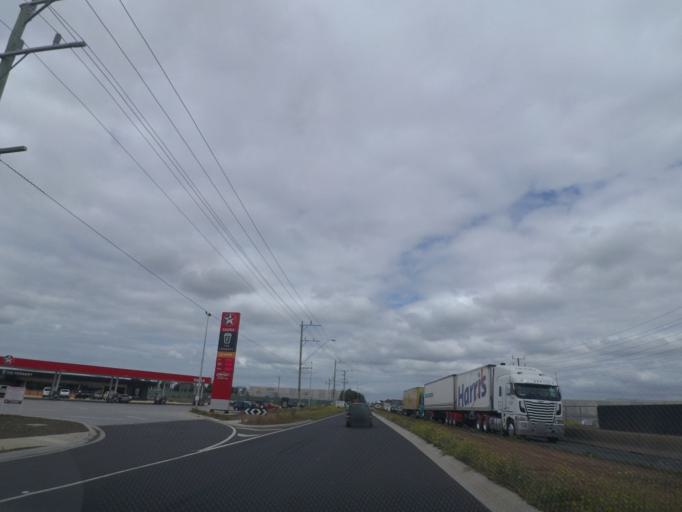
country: AU
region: Victoria
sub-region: Wyndham
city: Truganina
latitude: -37.8043
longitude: 144.7519
